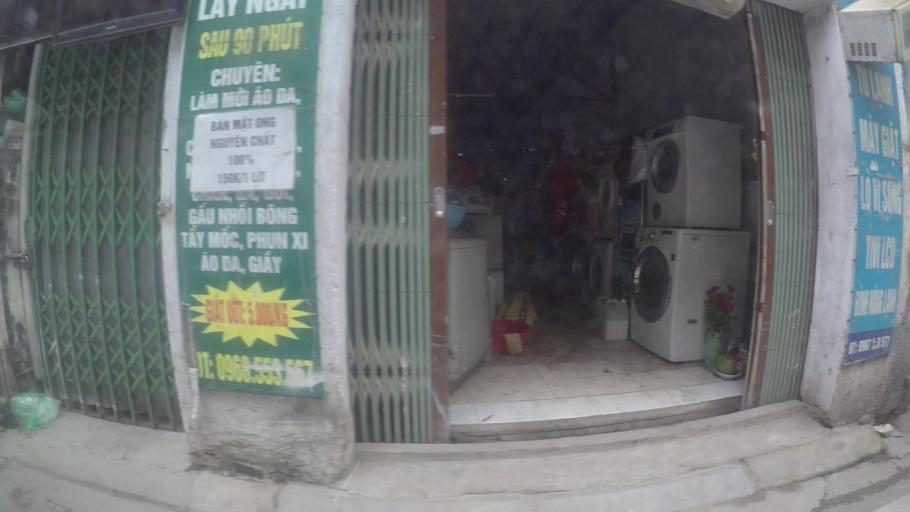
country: VN
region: Ha Noi
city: Tay Ho
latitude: 21.0611
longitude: 105.8357
